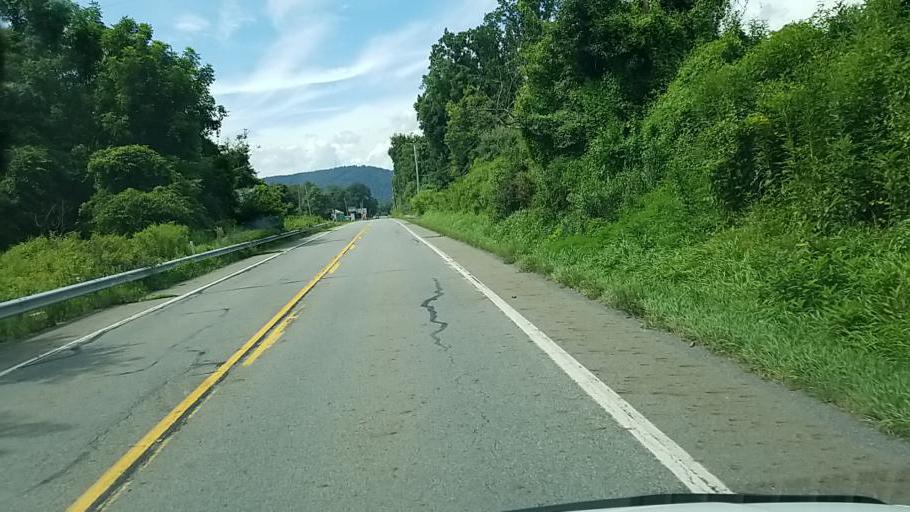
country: US
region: Pennsylvania
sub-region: Dauphin County
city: Millersburg
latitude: 40.5060
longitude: -76.9559
